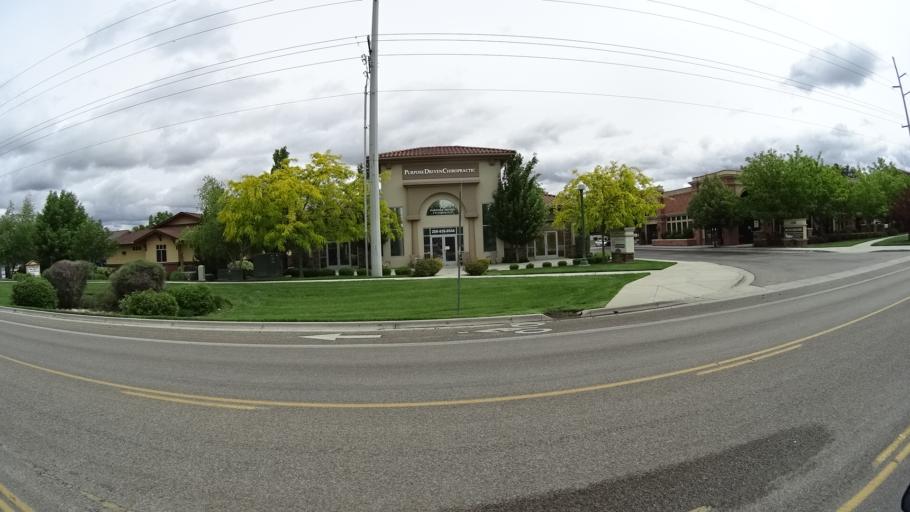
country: US
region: Idaho
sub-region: Ada County
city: Eagle
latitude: 43.6929
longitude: -116.3394
